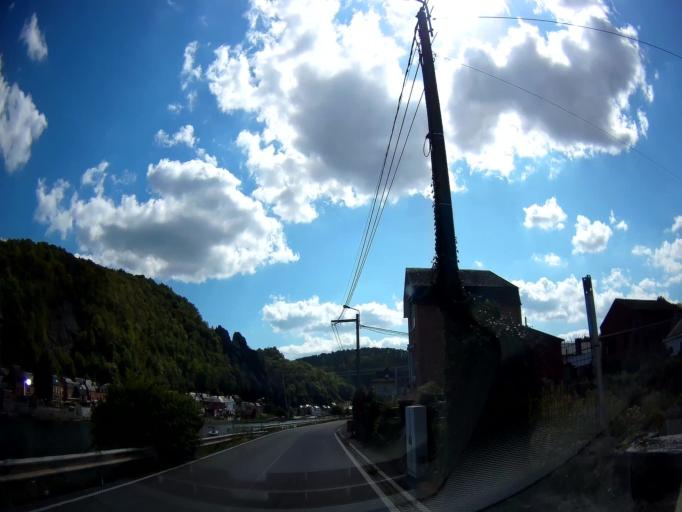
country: BE
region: Wallonia
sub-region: Province de Namur
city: Dinant
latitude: 50.2478
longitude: 4.9186
